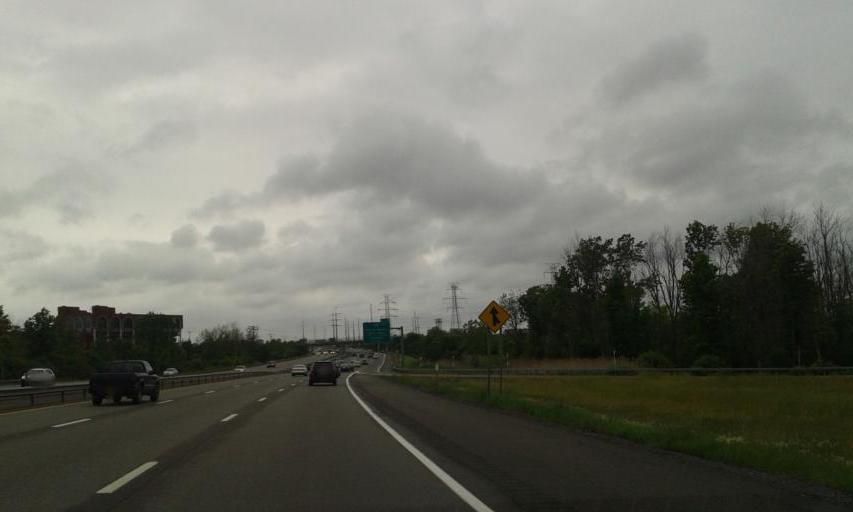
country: US
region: New York
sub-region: Erie County
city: Amherst
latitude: 42.9866
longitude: -78.7961
